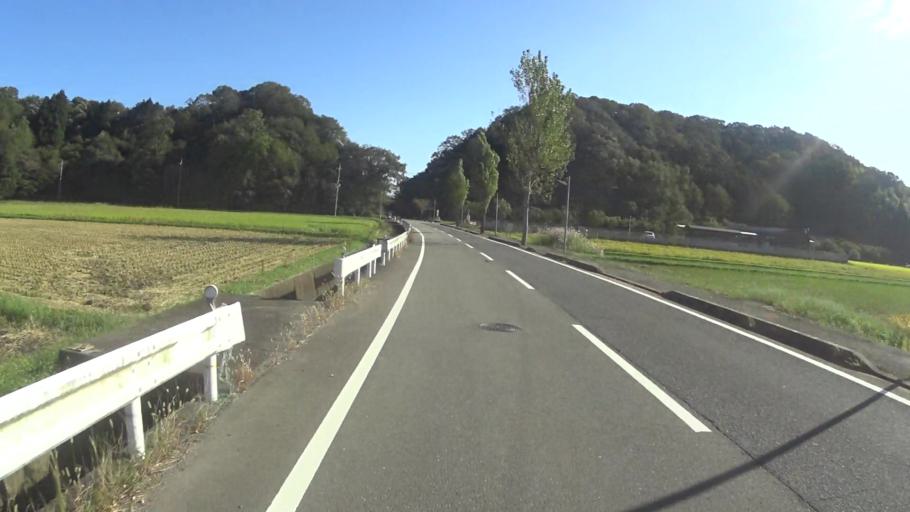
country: JP
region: Kyoto
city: Kameoka
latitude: 35.0730
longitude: 135.5659
